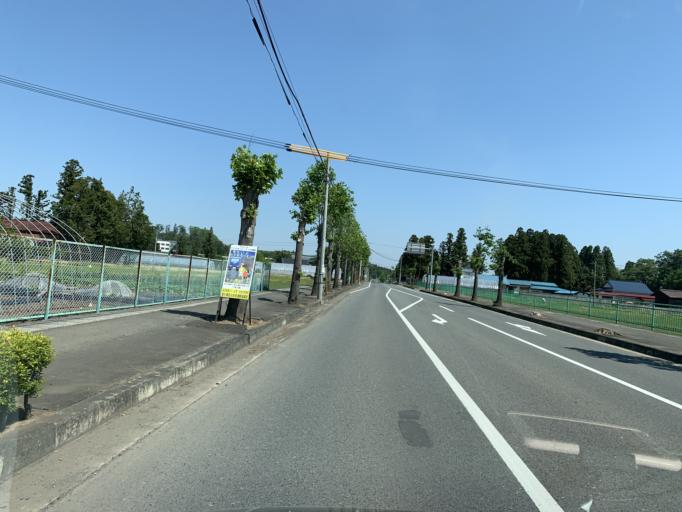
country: JP
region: Iwate
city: Mizusawa
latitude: 39.2014
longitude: 141.0950
